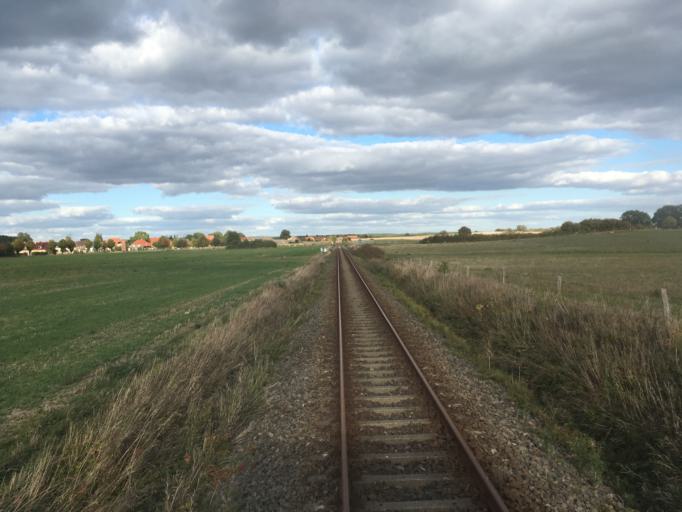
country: DE
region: Mecklenburg-Vorpommern
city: Malchow
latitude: 53.5142
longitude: 12.4378
